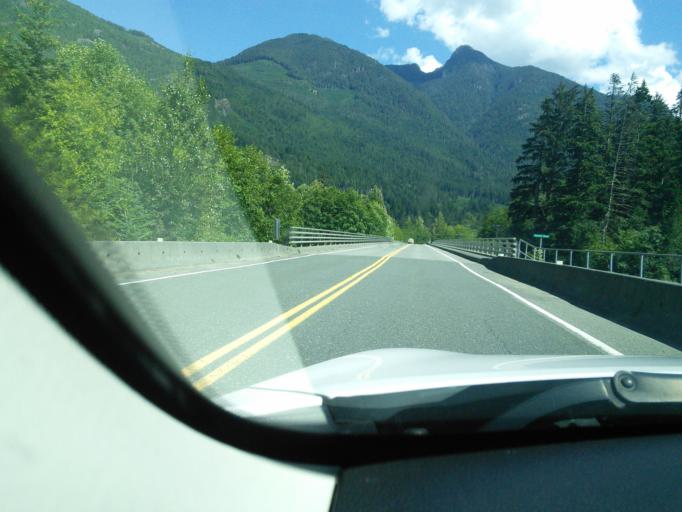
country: CA
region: British Columbia
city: Campbell River
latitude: 50.3614
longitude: -125.9197
